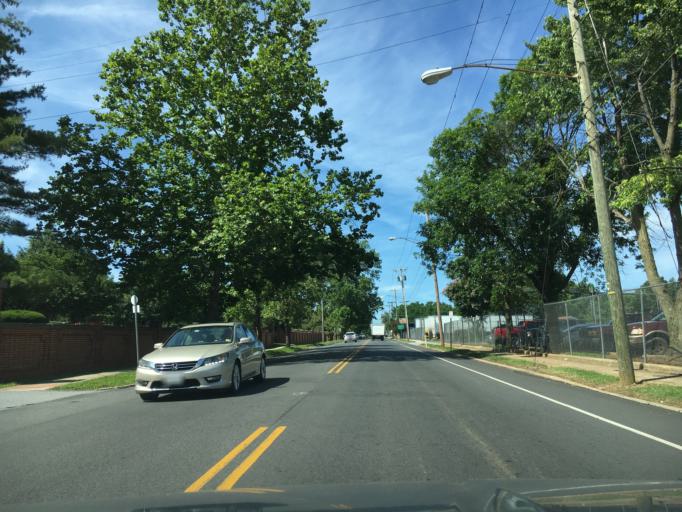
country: US
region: Virginia
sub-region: City of Lynchburg
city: West Lynchburg
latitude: 37.3977
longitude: -79.1643
